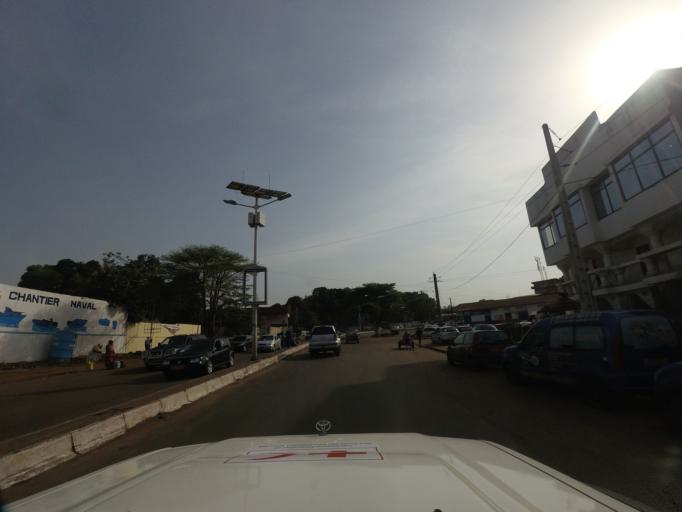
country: GN
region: Conakry
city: Conakry
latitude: 9.5571
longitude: -13.6687
